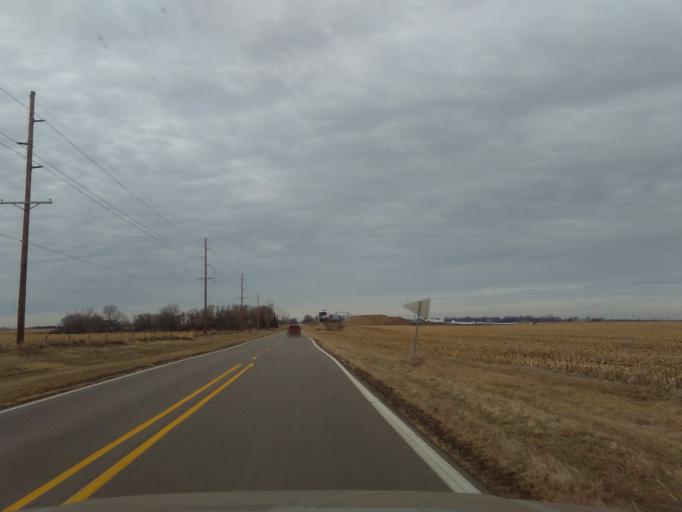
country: US
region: Nebraska
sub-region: Hall County
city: Grand Island
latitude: 40.7710
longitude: -98.3463
